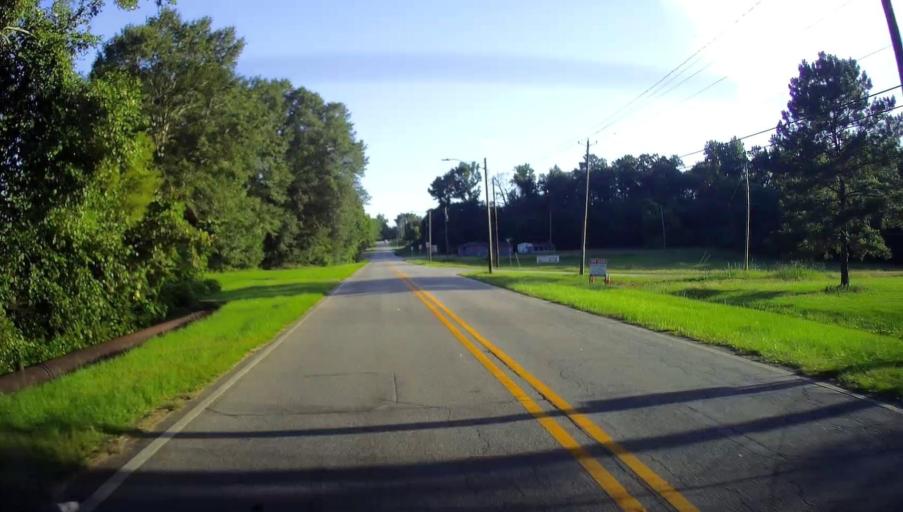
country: US
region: Georgia
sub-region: Muscogee County
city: Columbus
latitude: 32.4347
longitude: -85.0123
